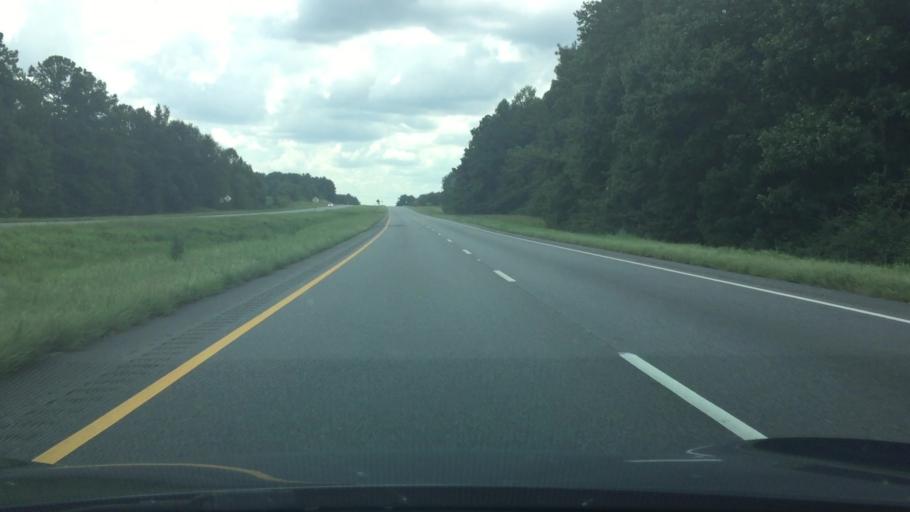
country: US
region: Alabama
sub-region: Pike County
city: Troy
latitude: 31.8894
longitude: -86.0084
